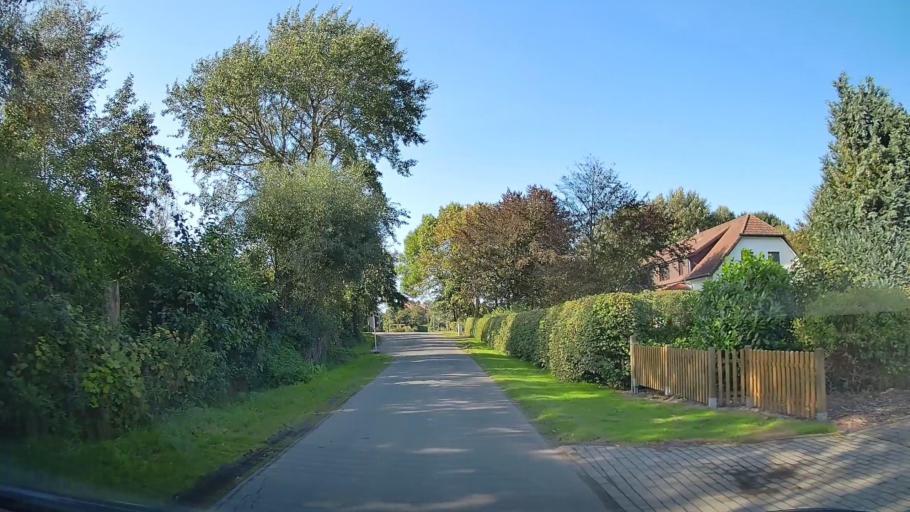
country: DE
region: Lower Saxony
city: Misselwarden
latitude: 53.6942
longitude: 8.4931
